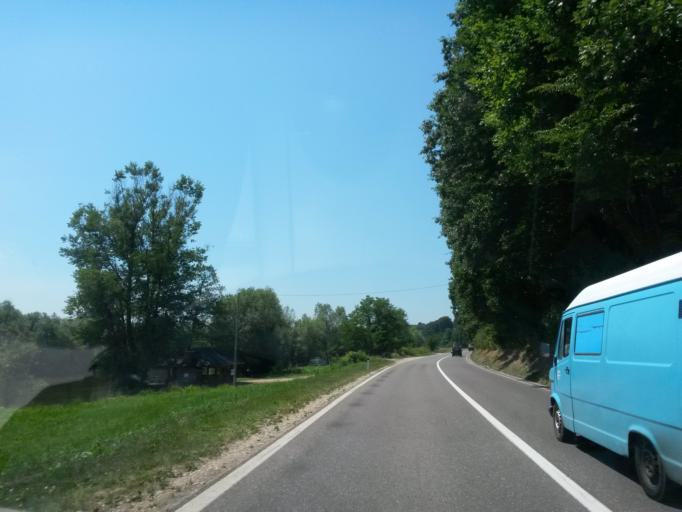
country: BA
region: Federation of Bosnia and Herzegovina
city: Odzak
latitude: 44.9603
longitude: 18.2215
